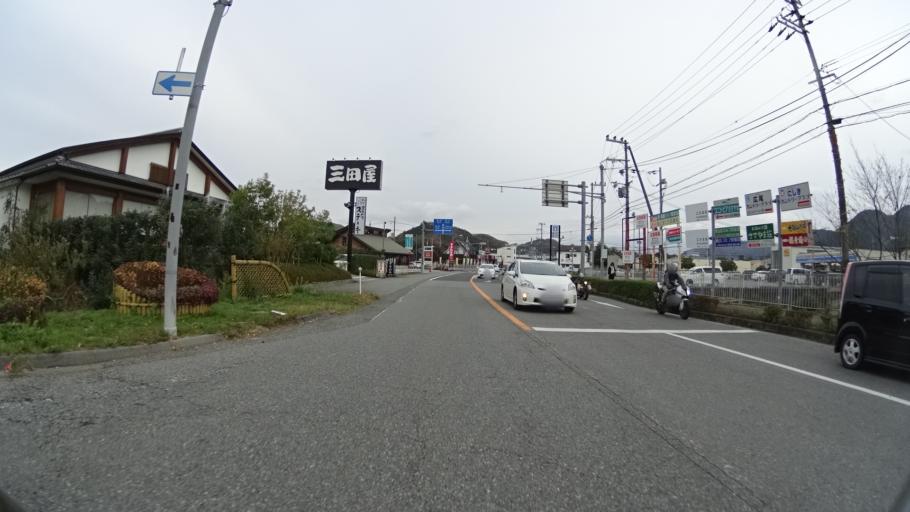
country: JP
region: Hyogo
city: Sasayama
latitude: 35.0641
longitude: 135.1795
